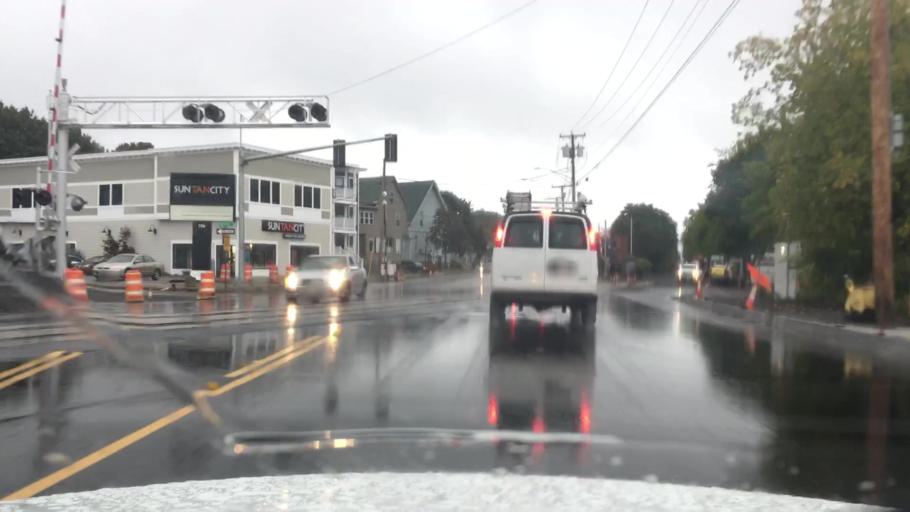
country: US
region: Maine
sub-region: Cumberland County
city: Portland
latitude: 43.6726
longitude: -70.2850
